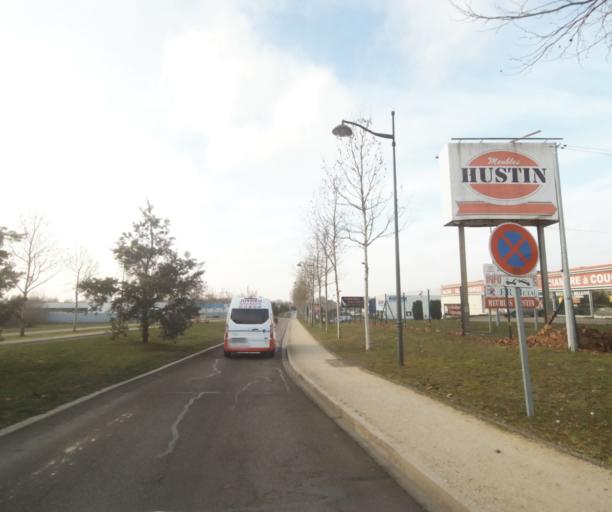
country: FR
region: Champagne-Ardenne
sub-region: Departement de la Haute-Marne
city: Bettancourt-la-Ferree
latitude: 48.6520
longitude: 4.9625
